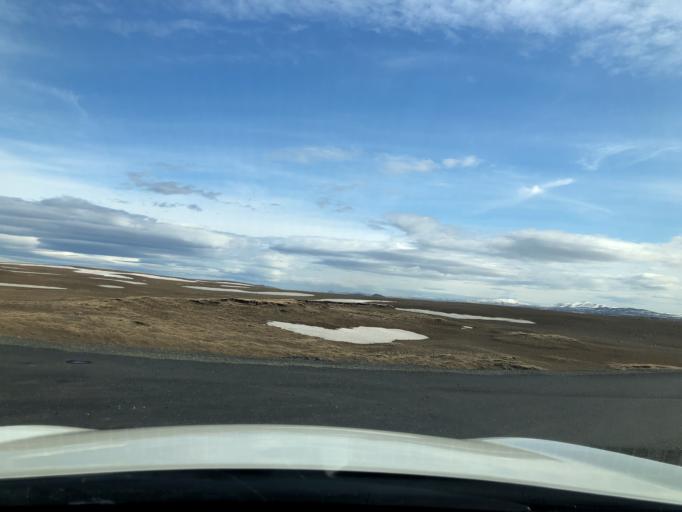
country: IS
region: Northeast
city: Husavik
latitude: 65.8149
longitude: -16.4425
